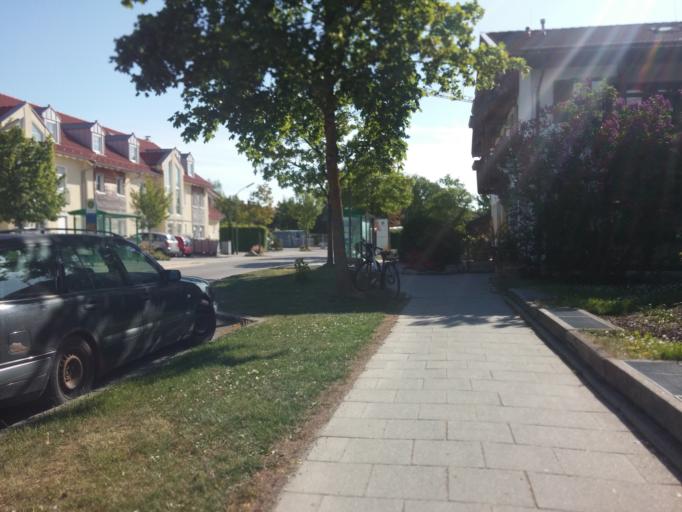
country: DE
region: Bavaria
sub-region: Upper Bavaria
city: Vaterstetten
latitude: 48.1102
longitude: 11.7687
